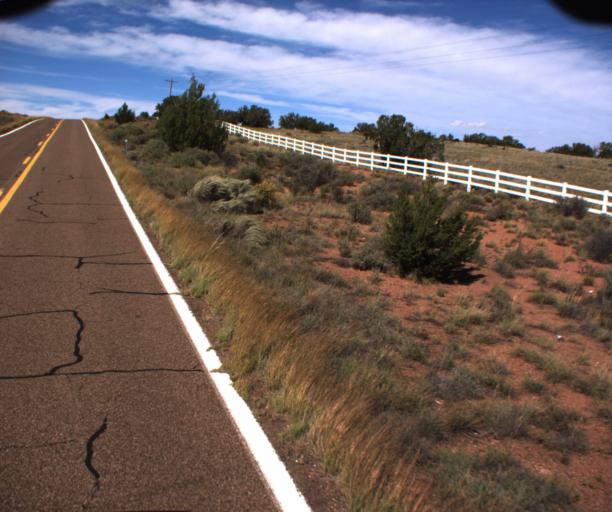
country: US
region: Arizona
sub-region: Apache County
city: Saint Johns
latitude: 34.5800
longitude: -109.6402
